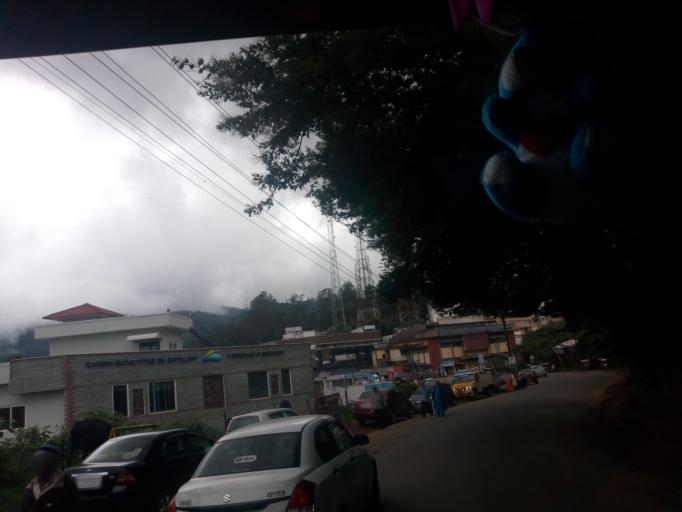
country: IN
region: Tamil Nadu
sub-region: Nilgiri
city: Ooty
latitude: 11.4088
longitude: 76.7077
